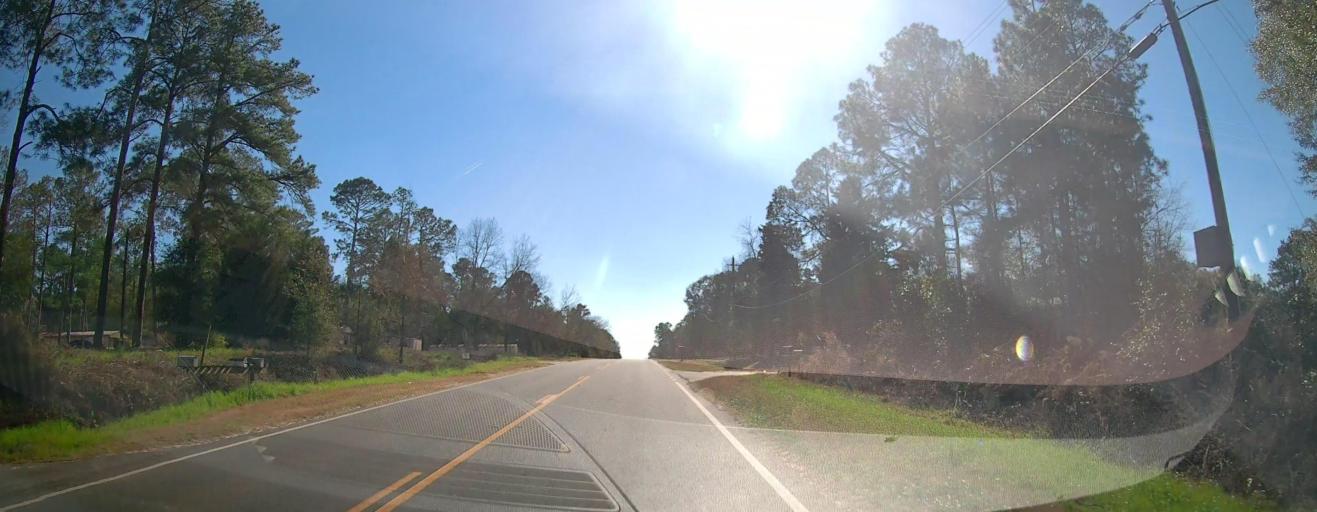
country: US
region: Georgia
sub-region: Macon County
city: Oglethorpe
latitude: 32.2768
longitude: -84.0766
